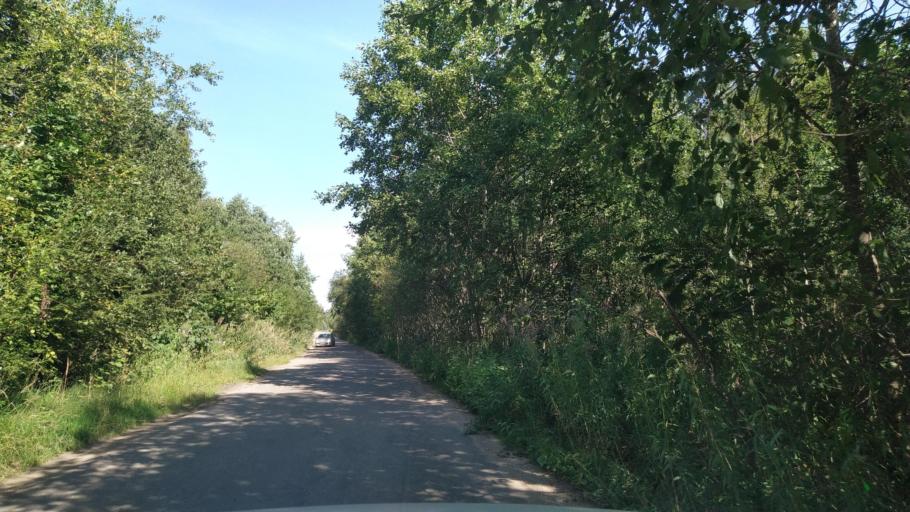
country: RU
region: Leningrad
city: Siverskiy
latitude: 59.2811
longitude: 30.0289
